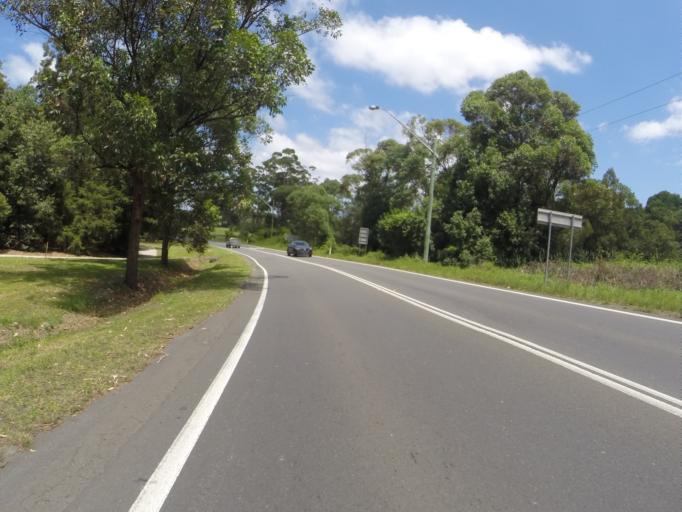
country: AU
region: New South Wales
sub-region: Shoalhaven Shire
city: Berry
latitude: -34.7744
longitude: 150.6862
